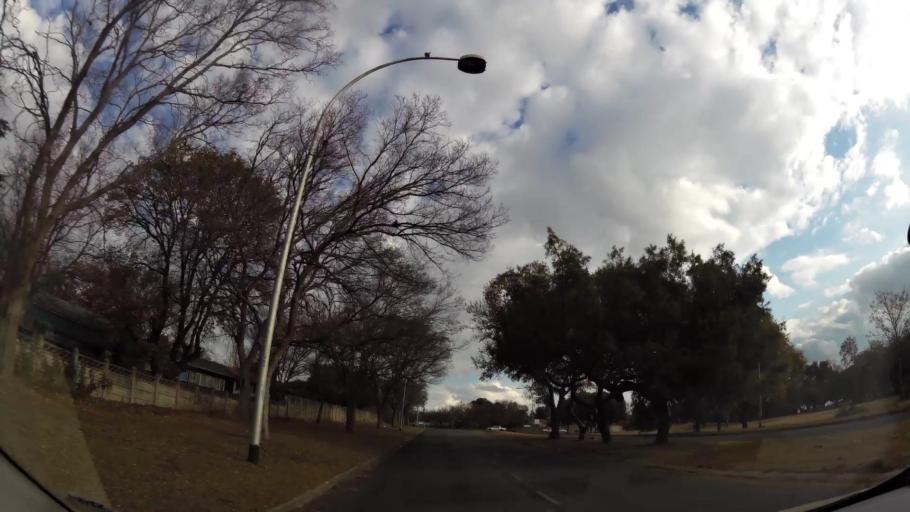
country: ZA
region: Orange Free State
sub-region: Fezile Dabi District Municipality
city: Sasolburg
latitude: -26.8101
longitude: 27.8099
